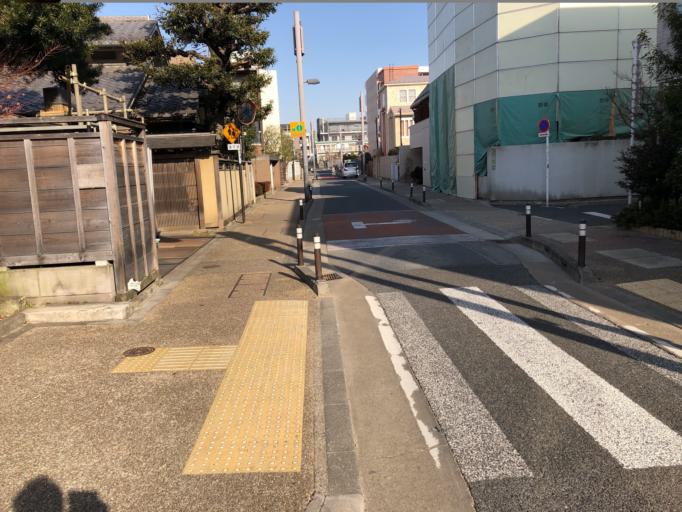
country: JP
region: Tokyo
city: Tokyo
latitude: 35.7269
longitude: 139.7607
